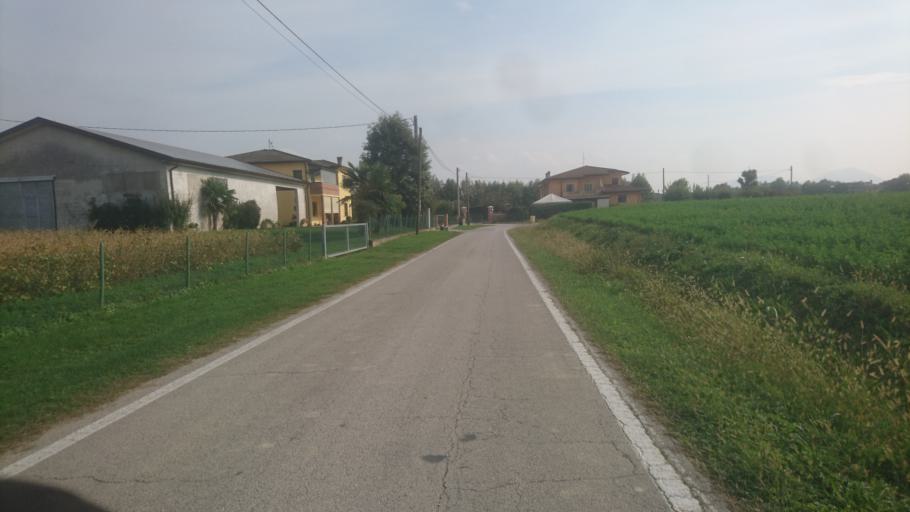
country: IT
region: Veneto
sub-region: Provincia di Vicenza
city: Montegalda
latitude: 45.4606
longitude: 11.6559
